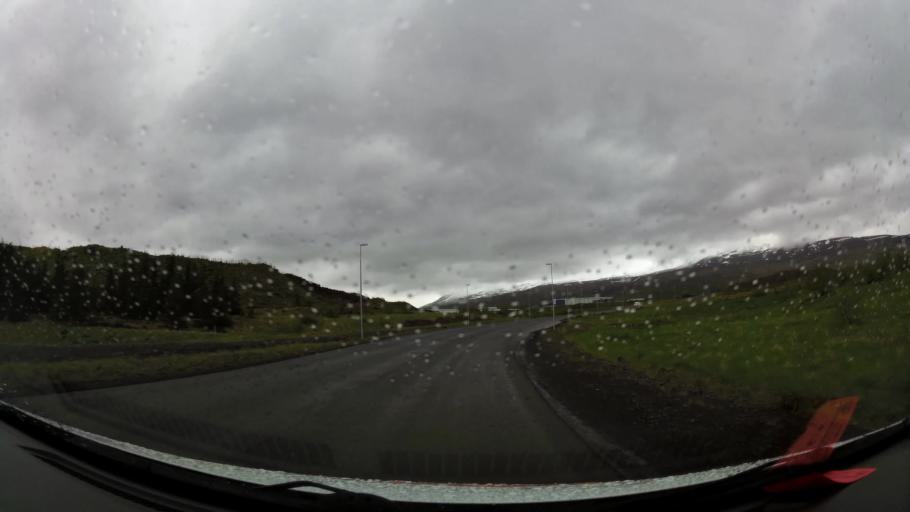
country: IS
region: Northeast
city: Akureyri
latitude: 65.7035
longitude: -18.1270
